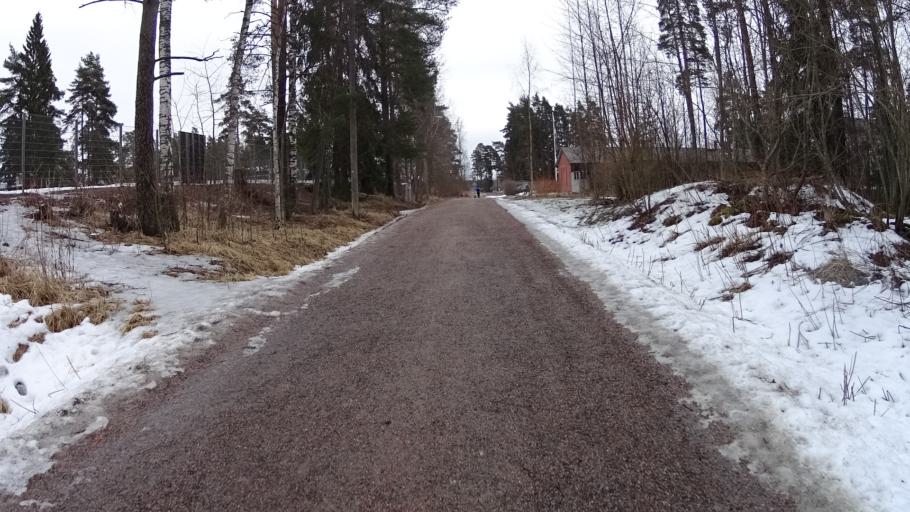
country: FI
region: Uusimaa
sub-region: Helsinki
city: Kilo
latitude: 60.2381
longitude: 24.8045
